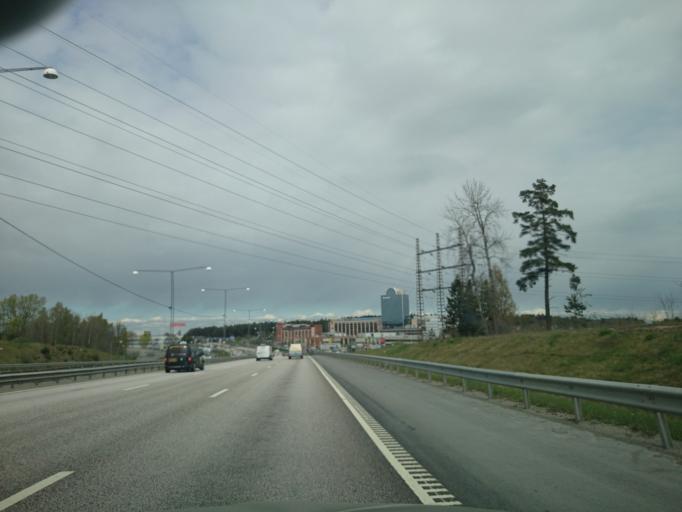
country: SE
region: Stockholm
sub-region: Upplands Vasby Kommun
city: Upplands Vaesby
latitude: 59.4940
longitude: 17.9218
